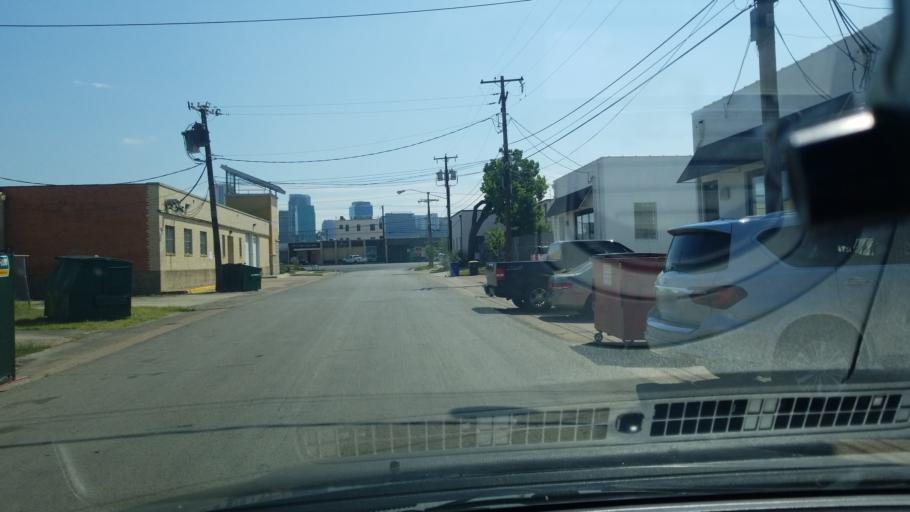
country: US
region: Texas
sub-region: Dallas County
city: Dallas
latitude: 32.7884
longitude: -96.8207
